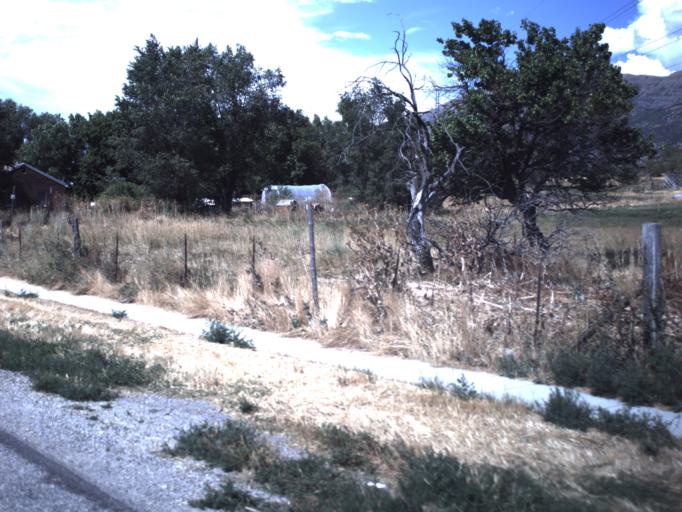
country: US
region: Utah
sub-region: Box Elder County
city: Honeyville
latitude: 41.6234
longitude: -112.0726
